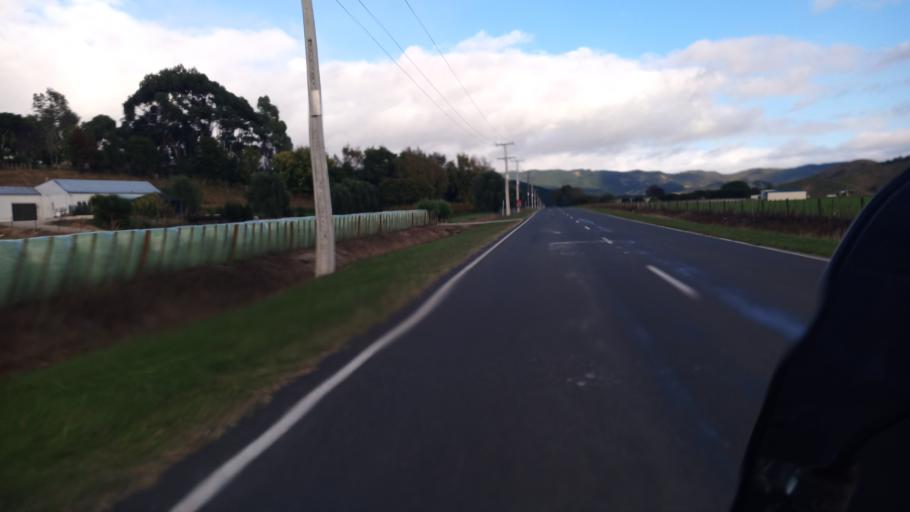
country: NZ
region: Gisborne
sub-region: Gisborne District
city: Gisborne
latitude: -38.6331
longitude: 177.8708
